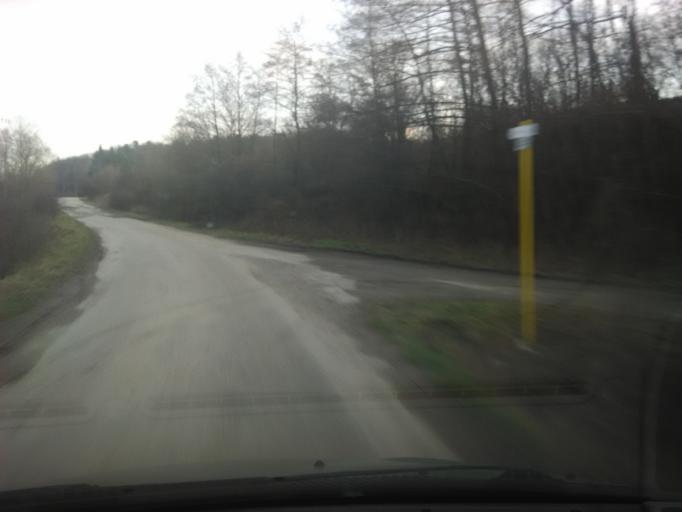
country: SK
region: Nitriansky
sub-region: Okres Nitra
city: Nitra
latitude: 48.3940
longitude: 18.2078
